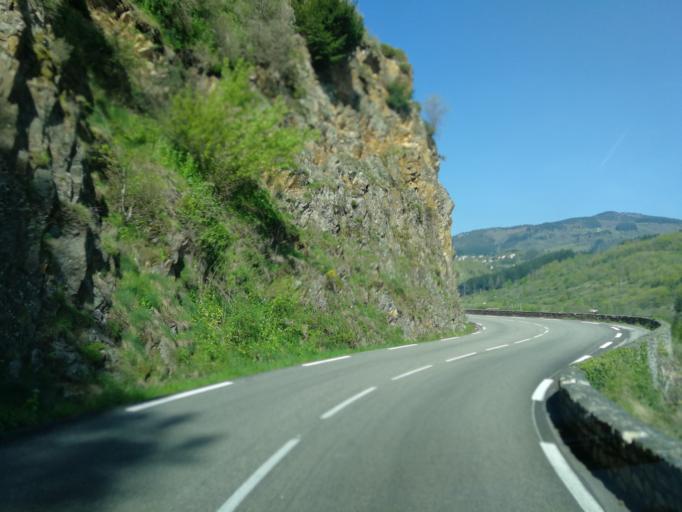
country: FR
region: Rhone-Alpes
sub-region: Departement de l'Ardeche
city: Le Cheylard
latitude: 44.9066
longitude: 4.4718
